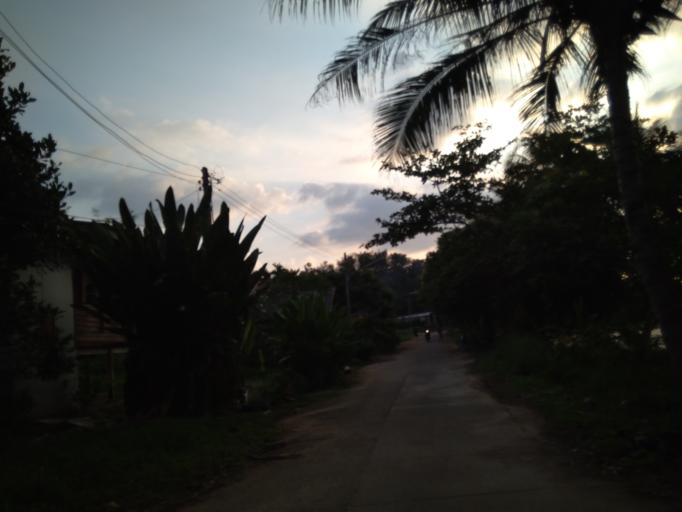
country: TH
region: Phangnga
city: Ko Yao
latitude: 8.1641
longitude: 98.6123
